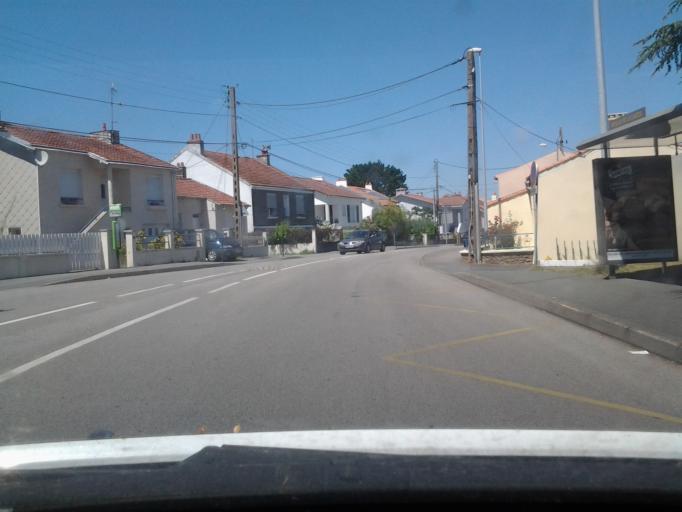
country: FR
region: Pays de la Loire
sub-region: Departement de la Vendee
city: La Roche-sur-Yon
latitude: 46.6584
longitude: -1.4318
